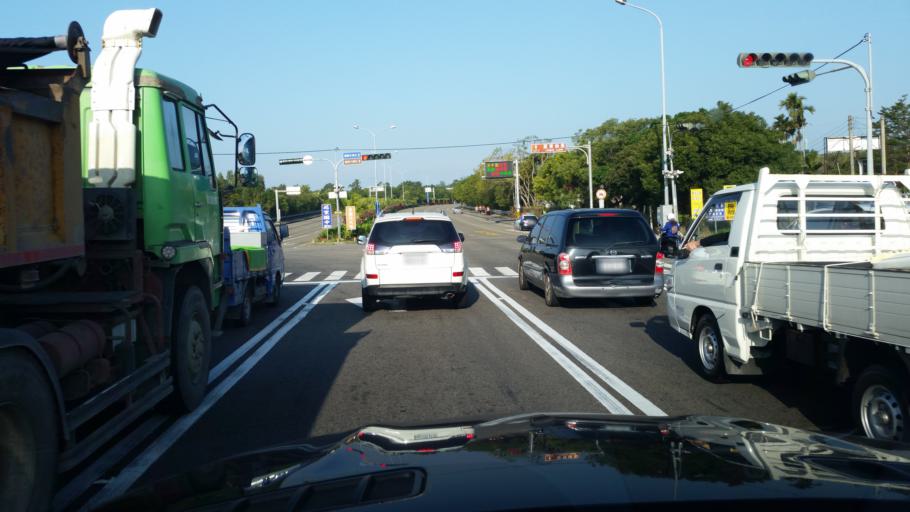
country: TW
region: Taiwan
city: Fengyuan
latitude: 24.3151
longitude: 120.6981
